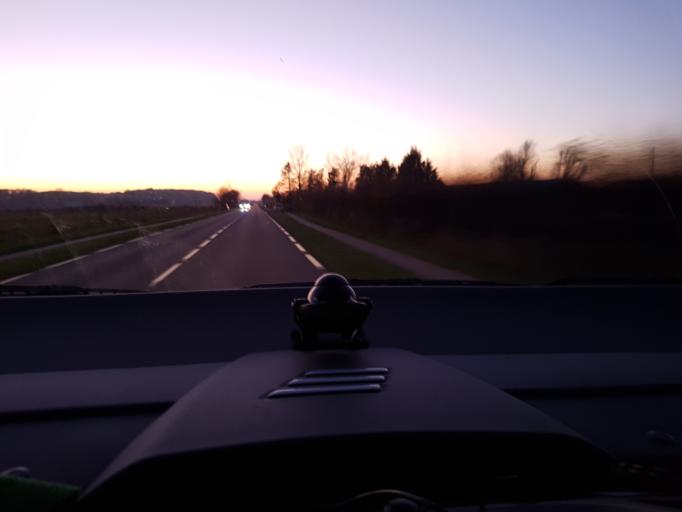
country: FR
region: Picardie
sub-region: Departement de la Somme
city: Saint-Valery-sur-Somme
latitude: 50.1742
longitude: 1.6781
